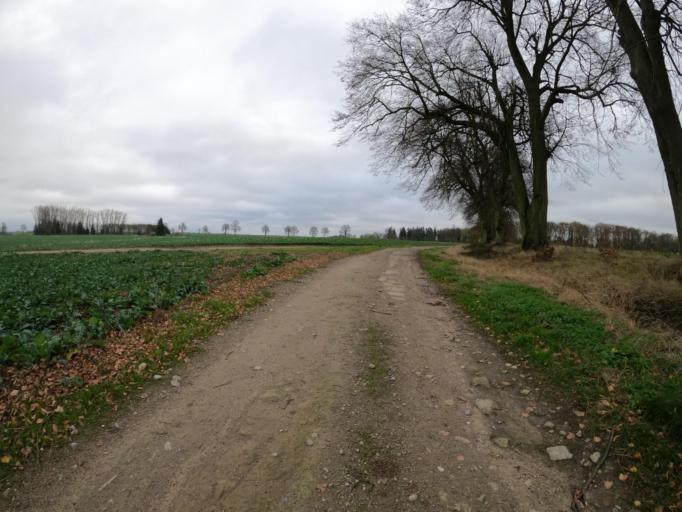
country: PL
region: West Pomeranian Voivodeship
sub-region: Powiat walecki
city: Tuczno
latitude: 53.2733
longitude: 16.1802
